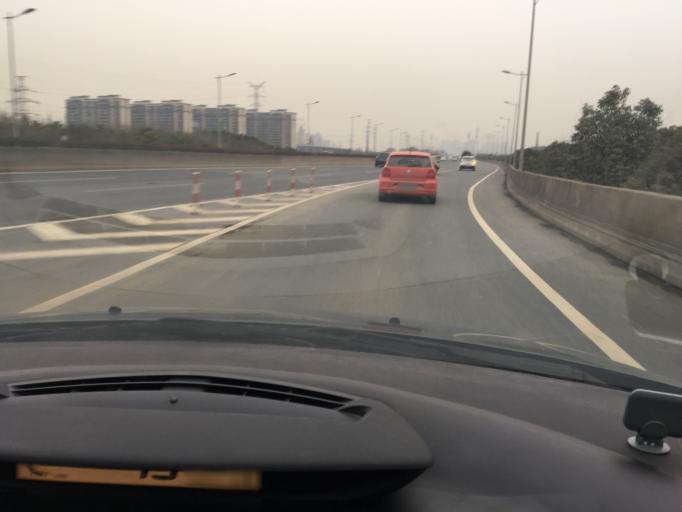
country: CN
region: Hubei
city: Hongqi
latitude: 30.5993
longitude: 114.4272
